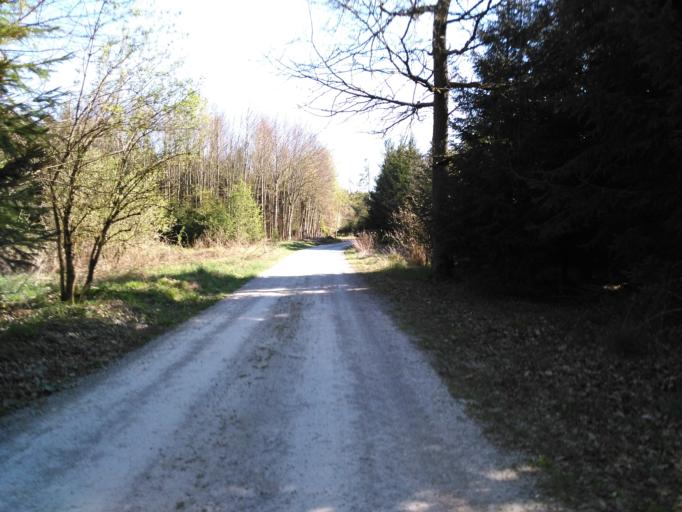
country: DE
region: Bavaria
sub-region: Upper Bavaria
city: Landsberied
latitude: 48.2008
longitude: 11.2041
